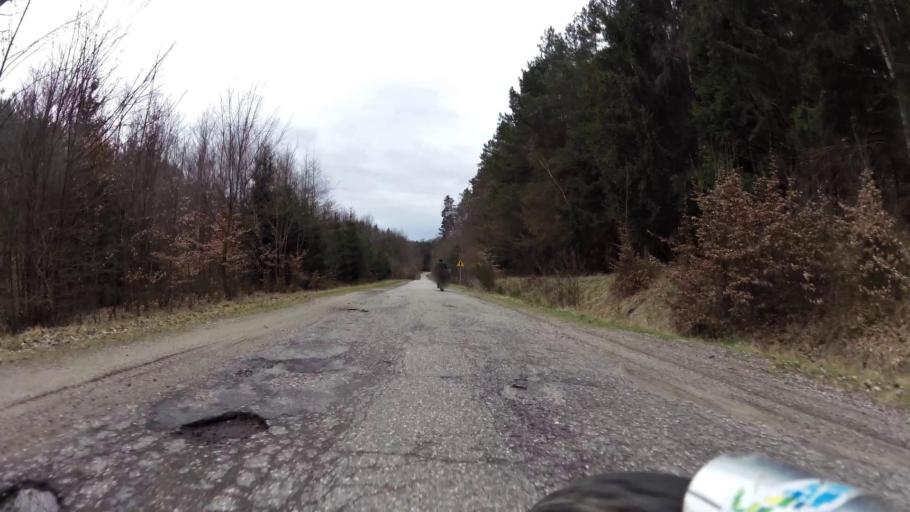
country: PL
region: Pomeranian Voivodeship
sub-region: Powiat bytowski
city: Trzebielino
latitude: 54.0867
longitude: 17.1344
